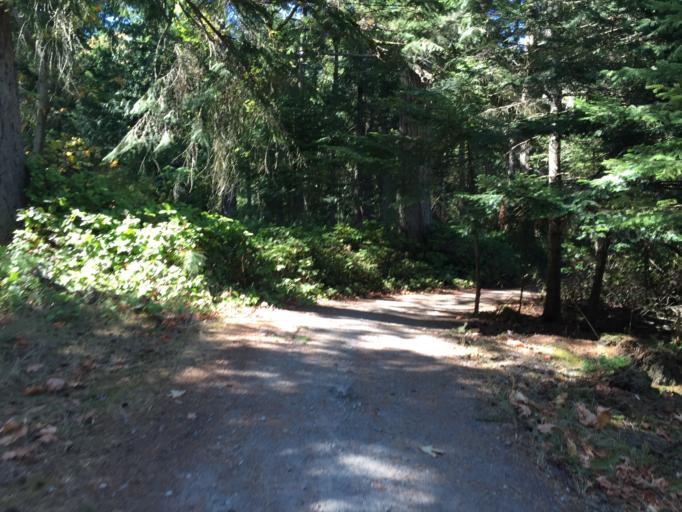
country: CA
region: British Columbia
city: Nanaimo
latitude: 49.1938
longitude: -123.9276
